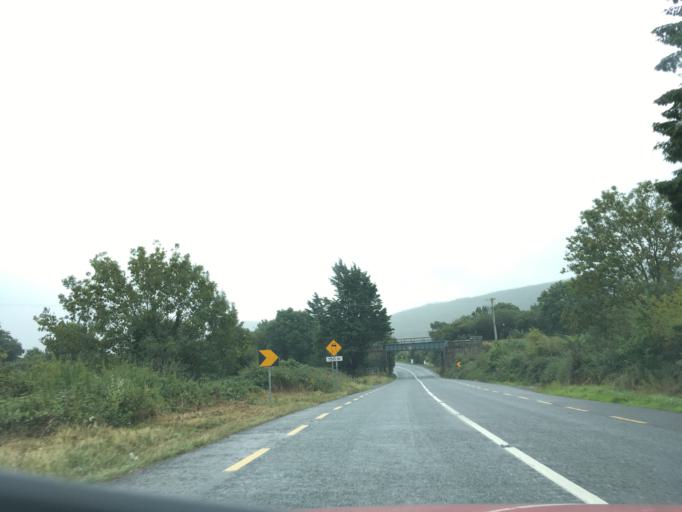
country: IE
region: Munster
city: Carrick-on-Suir
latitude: 52.3549
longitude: -7.4763
